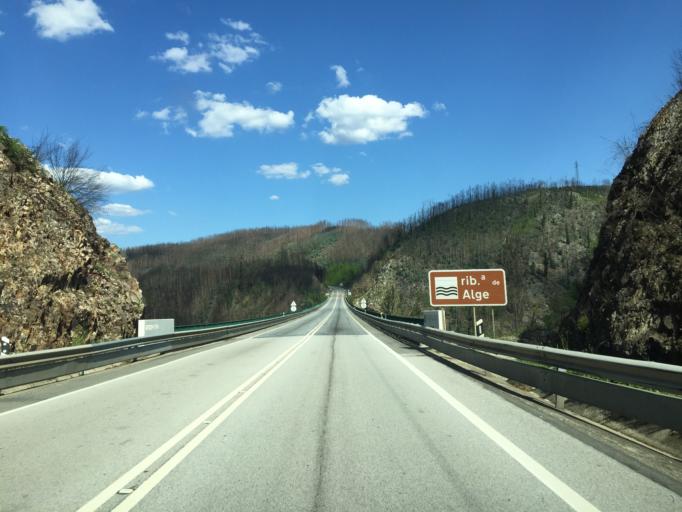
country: PT
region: Leiria
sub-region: Figueiro Dos Vinhos
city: Figueiro dos Vinhos
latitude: 39.9273
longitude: -8.3104
